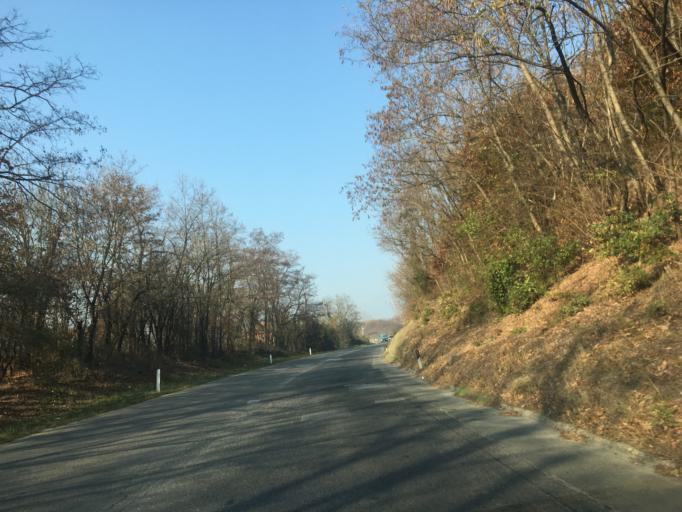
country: XK
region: Pec
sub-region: Komuna e Pejes
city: Kosuriq
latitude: 42.6388
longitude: 20.4287
